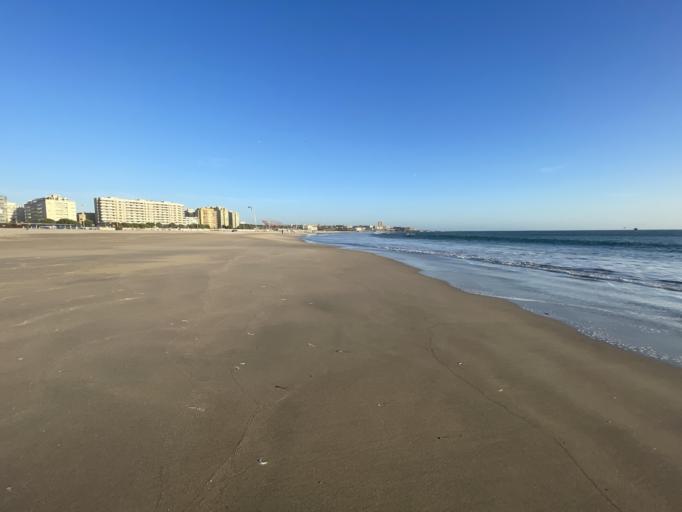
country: PT
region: Porto
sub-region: Matosinhos
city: Matosinhos
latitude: 41.1771
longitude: -8.6948
